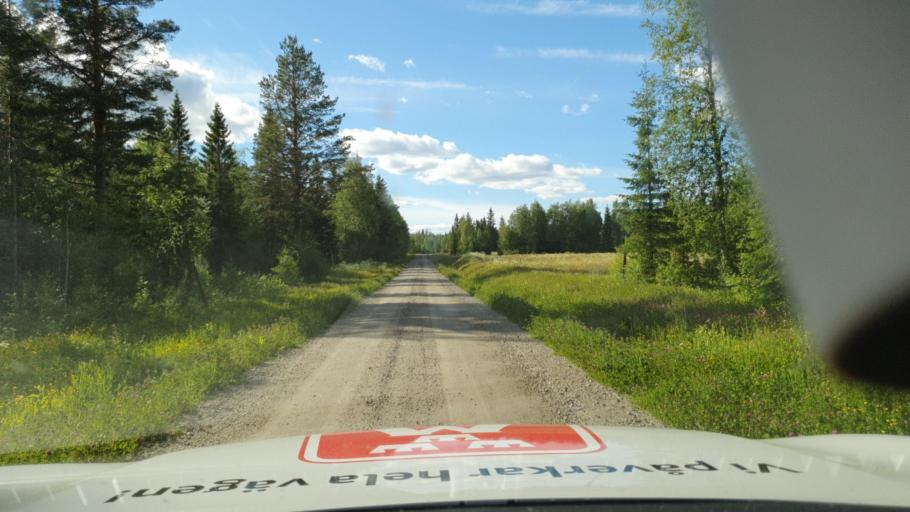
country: SE
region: Vaesterbotten
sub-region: Lycksele Kommun
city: Soderfors
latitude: 64.4839
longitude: 18.2815
